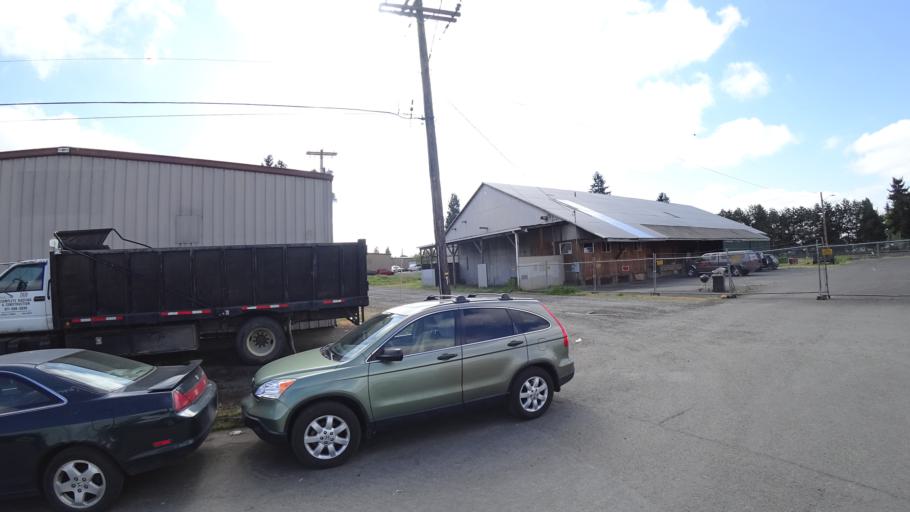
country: US
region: Oregon
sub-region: Washington County
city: Hillsboro
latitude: 45.5170
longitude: -122.9882
